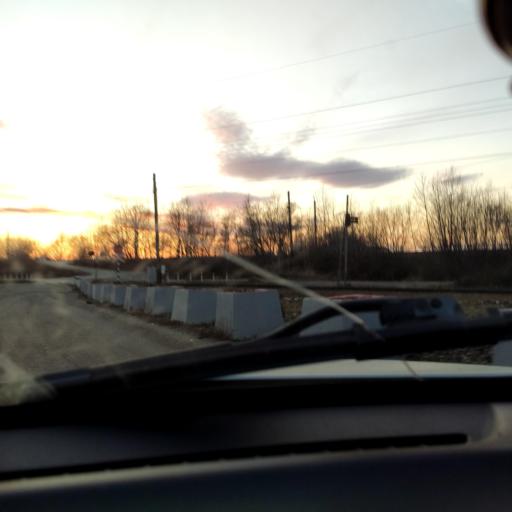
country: RU
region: Tatarstan
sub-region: Gorod Kazan'
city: Kazan
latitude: 55.7828
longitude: 49.0993
